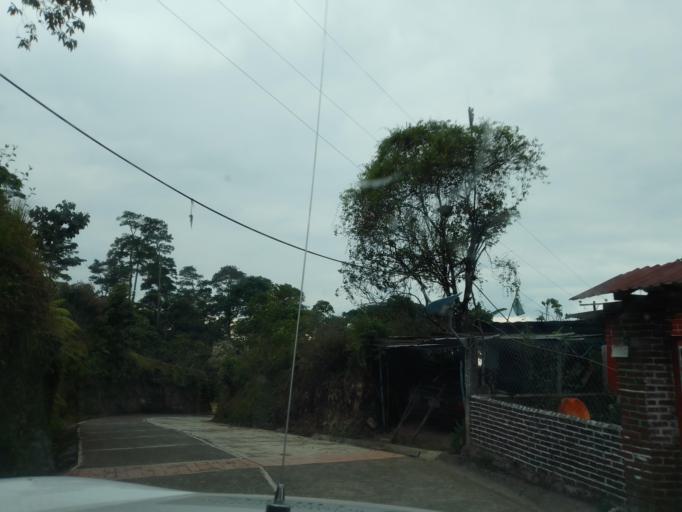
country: MX
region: Chiapas
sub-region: Union Juarez
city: Santo Domingo
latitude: 15.0564
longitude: -92.1114
